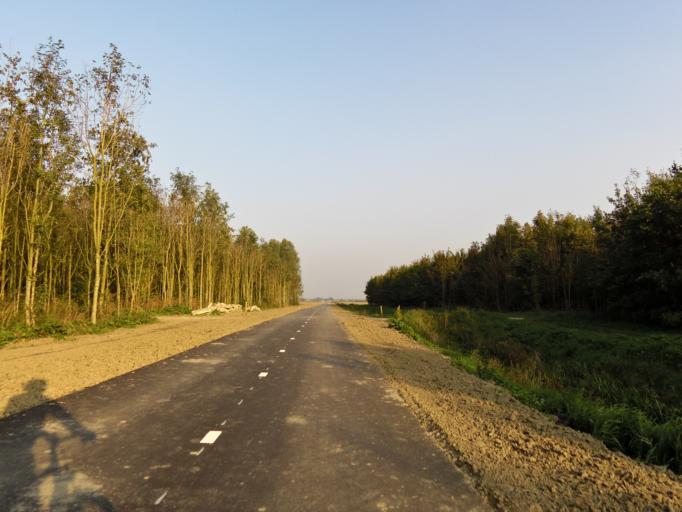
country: NL
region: South Holland
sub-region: Gemeente Waddinxveen
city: Groenswaard
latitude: 52.0729
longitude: 4.5983
